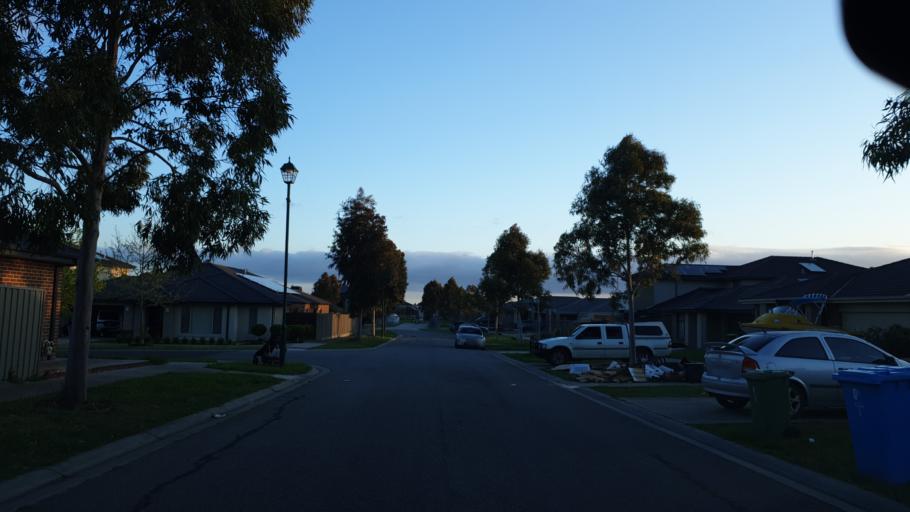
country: AU
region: Victoria
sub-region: Casey
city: Cranbourne East
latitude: -38.1080
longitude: 145.3085
